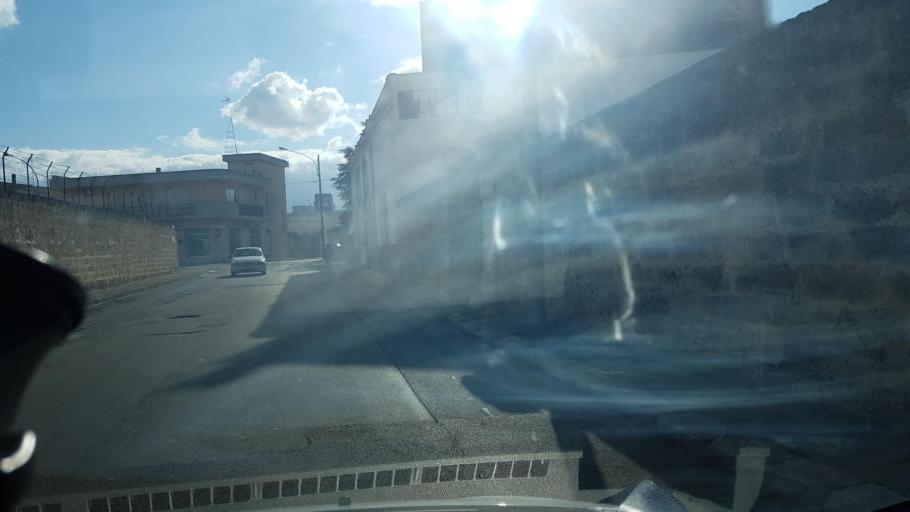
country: IT
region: Apulia
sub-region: Provincia di Lecce
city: Squinzano
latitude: 40.4402
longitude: 18.0374
